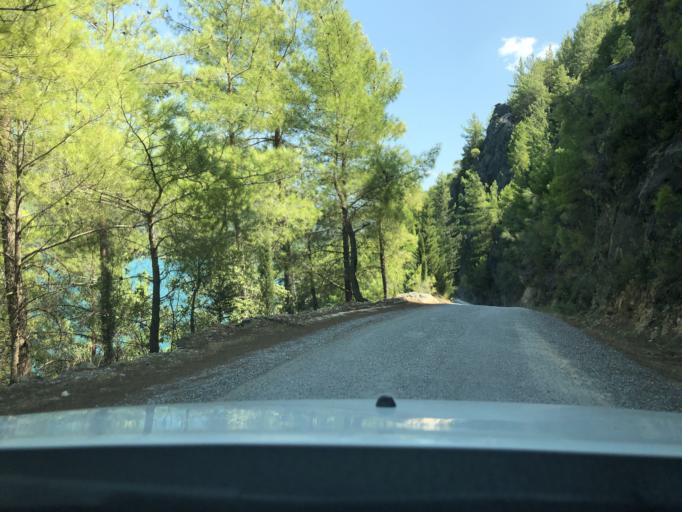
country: TR
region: Antalya
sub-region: Manavgat
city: Manavgat
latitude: 36.9068
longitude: 31.5563
